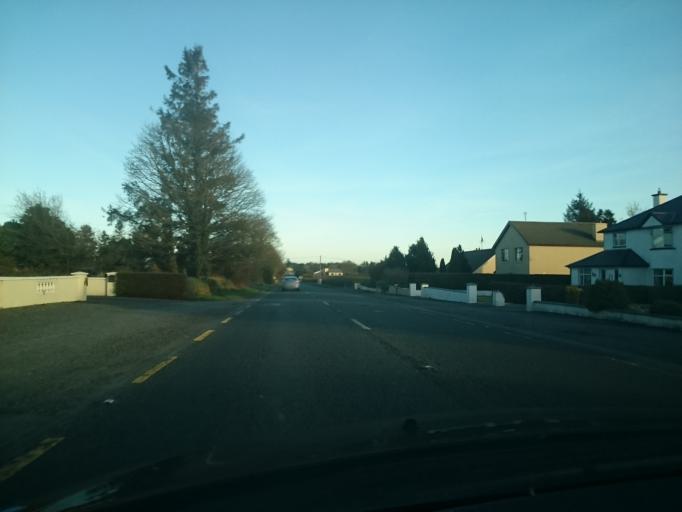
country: IE
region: Connaught
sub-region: Maigh Eo
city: Claremorris
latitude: 53.7424
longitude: -9.0155
